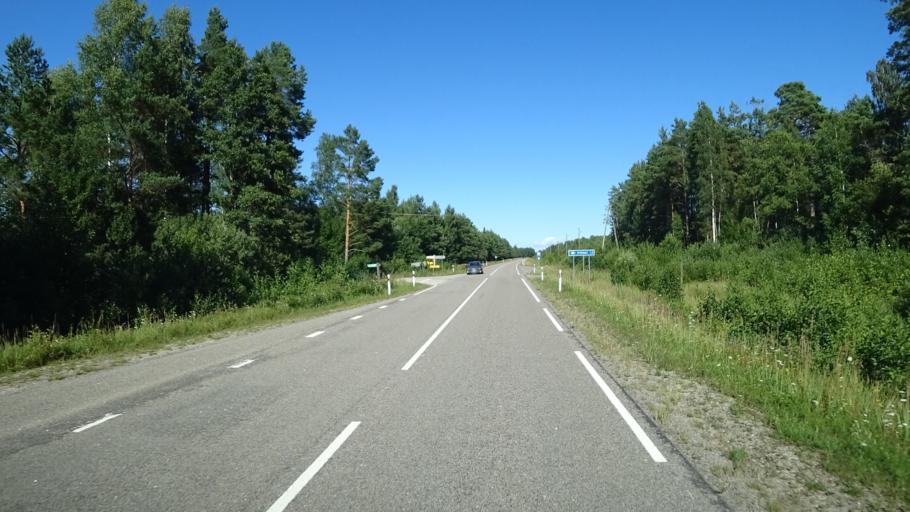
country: LV
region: Dundaga
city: Dundaga
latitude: 57.6940
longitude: 22.3959
